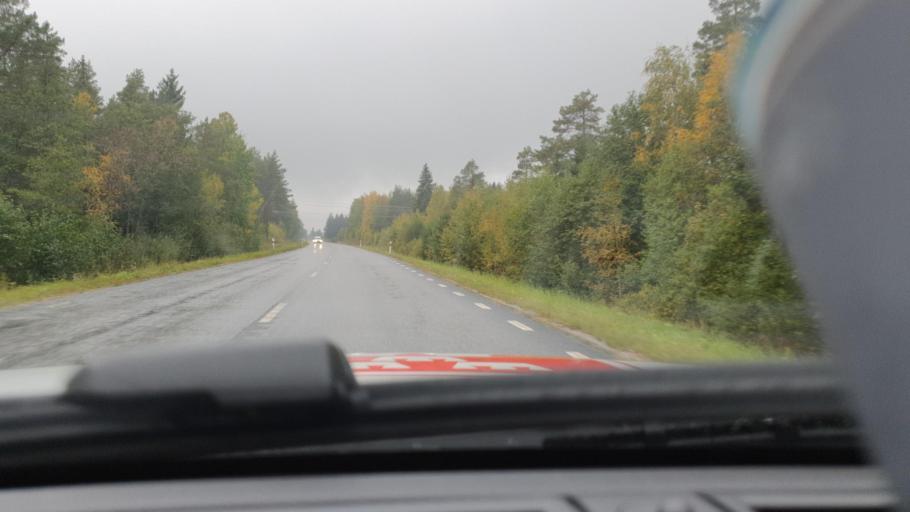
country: SE
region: Uppsala
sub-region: Tierps Kommun
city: Tierp
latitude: 60.3164
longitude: 17.5387
